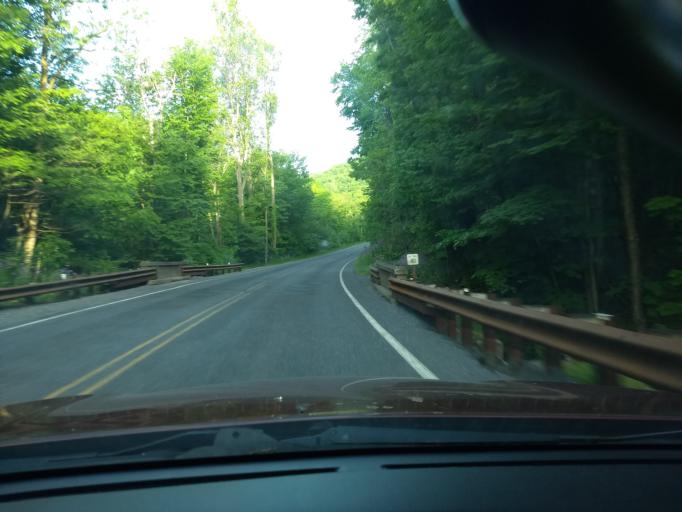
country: US
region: Pennsylvania
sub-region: Cambria County
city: Gallitzin
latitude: 40.5024
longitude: -78.5153
